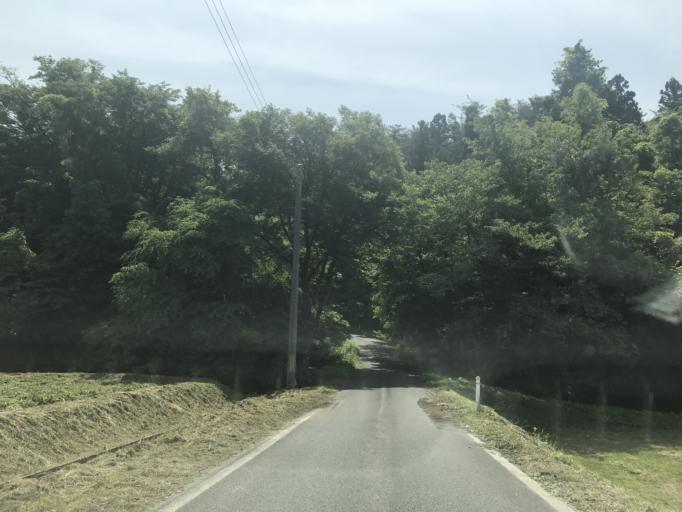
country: JP
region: Iwate
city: Ichinoseki
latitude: 38.9716
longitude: 141.2212
